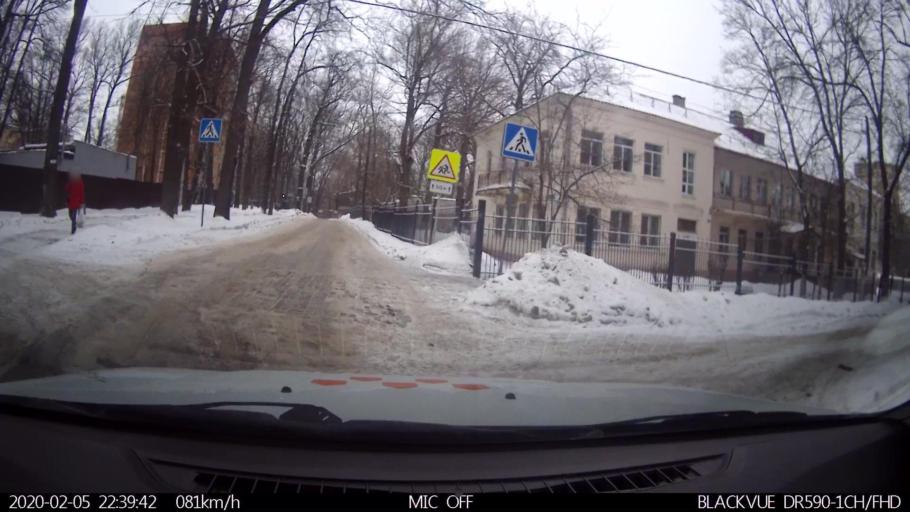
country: RU
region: Nizjnij Novgorod
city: Imeni Stepana Razina
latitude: 54.7258
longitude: 44.3071
